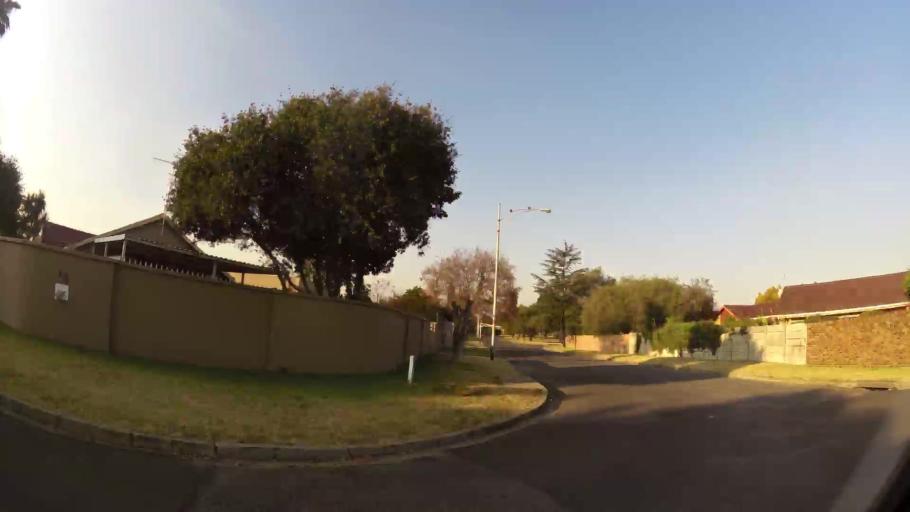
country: ZA
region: Gauteng
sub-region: Ekurhuleni Metropolitan Municipality
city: Springs
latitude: -26.2579
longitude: 28.3999
